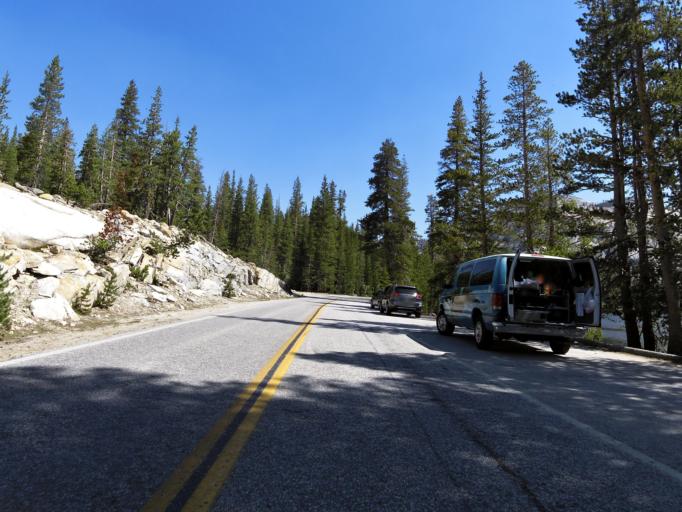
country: US
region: California
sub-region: Mariposa County
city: Yosemite Valley
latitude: 37.8297
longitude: -119.4679
